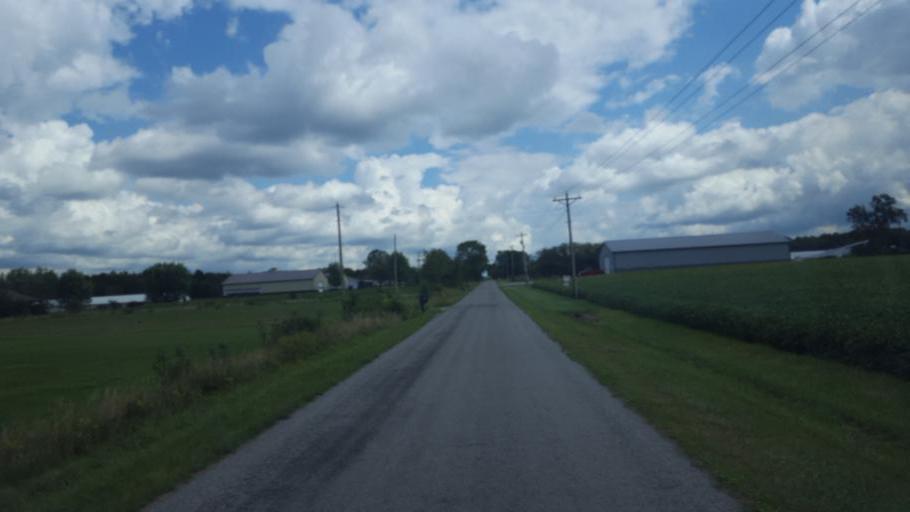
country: US
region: Ohio
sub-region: Huron County
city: Plymouth
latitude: 41.0453
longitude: -82.6182
